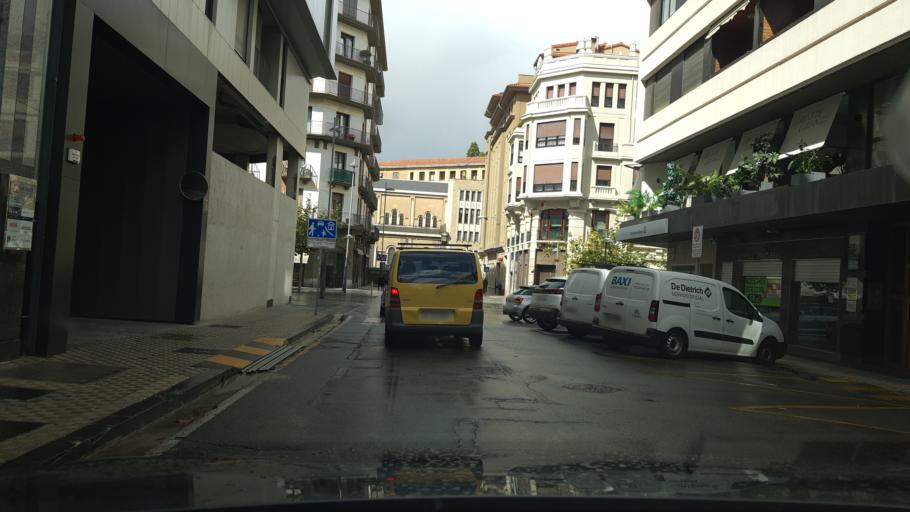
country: ES
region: Navarre
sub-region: Provincia de Navarra
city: Segundo Ensanche
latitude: 42.8141
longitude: -1.6416
